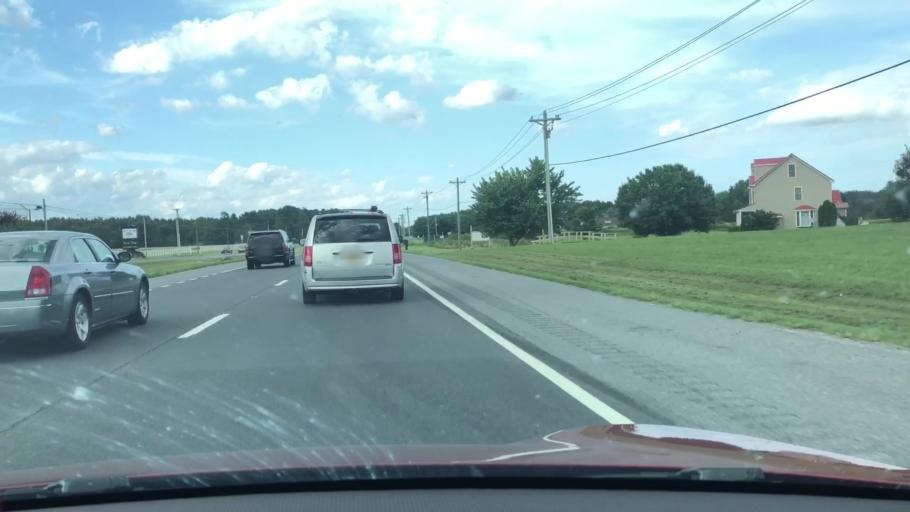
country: US
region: Delaware
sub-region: Sussex County
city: Bridgeville
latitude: 38.8235
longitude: -75.5853
